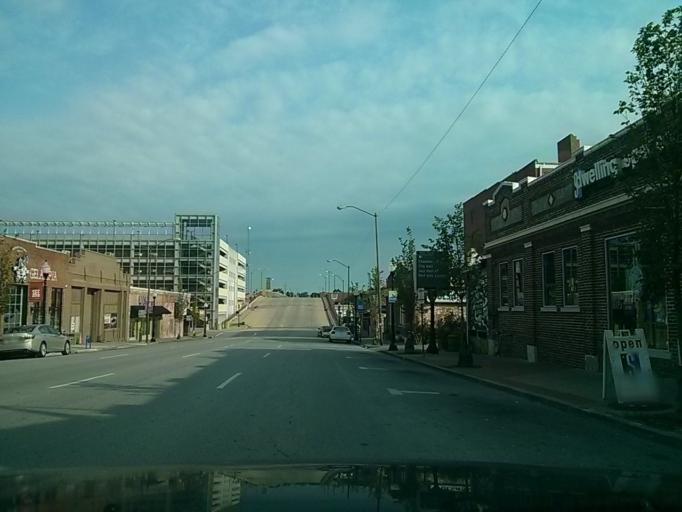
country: US
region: Oklahoma
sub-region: Tulsa County
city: Tulsa
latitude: 36.1557
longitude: -95.9880
